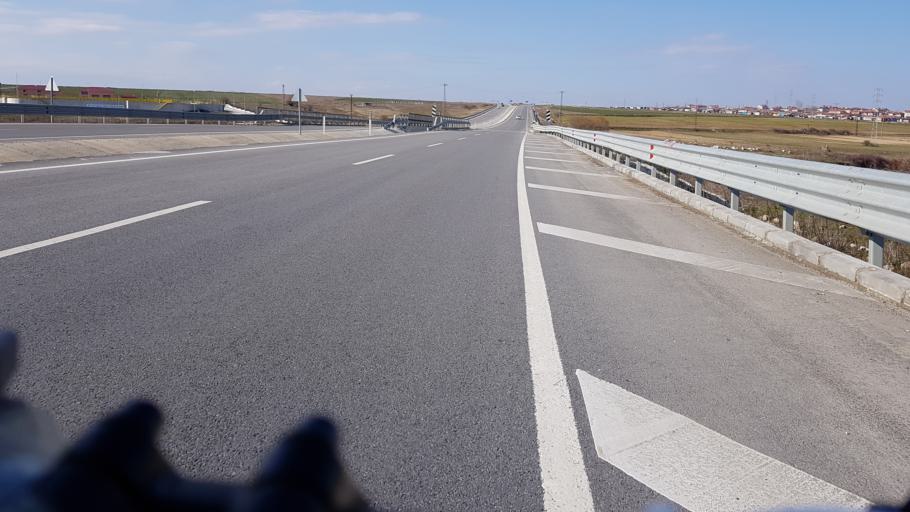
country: TR
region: Tekirdag
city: Saray
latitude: 41.4246
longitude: 27.9130
